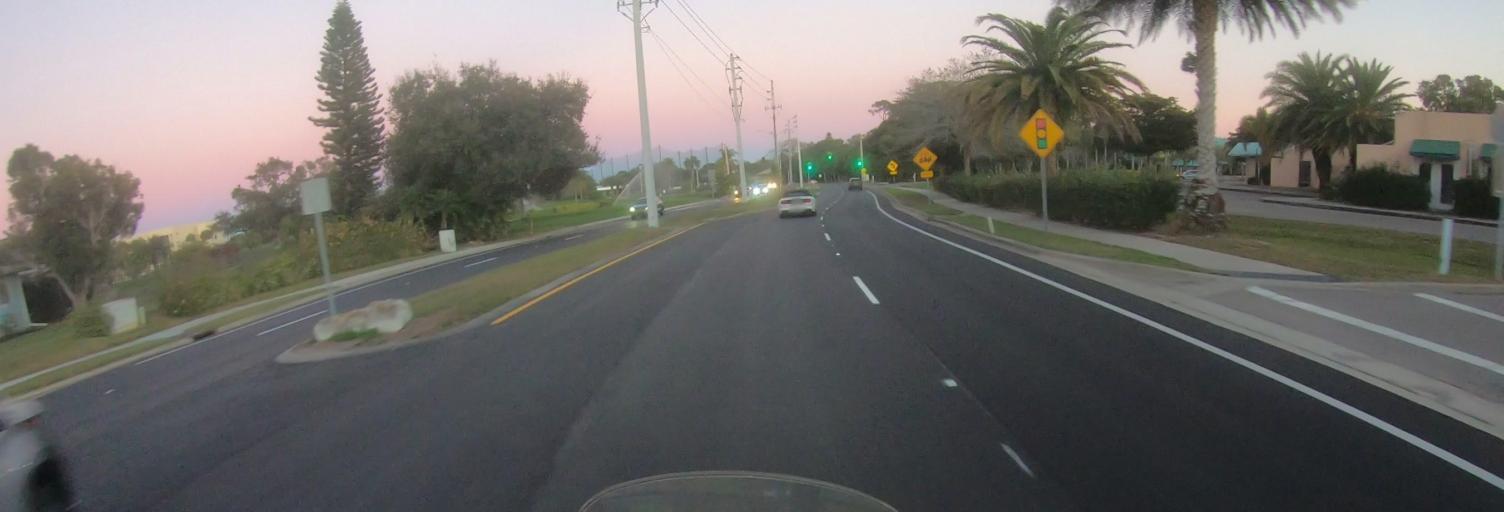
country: US
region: Florida
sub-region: Manatee County
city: Bayshore Gardens
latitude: 27.4293
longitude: -82.6064
